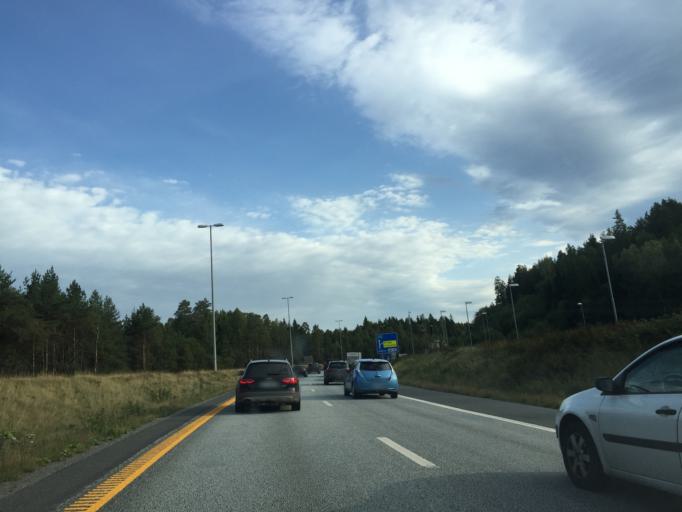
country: NO
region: Akershus
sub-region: Oppegard
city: Kolbotn
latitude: 59.8123
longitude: 10.8397
